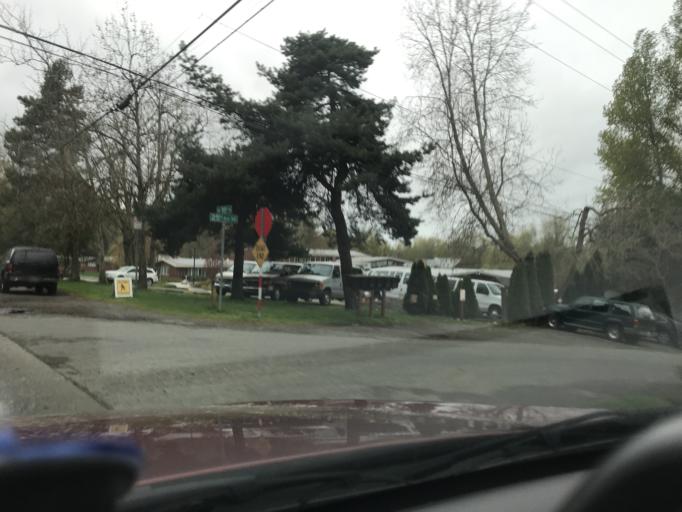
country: US
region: Washington
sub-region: King County
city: Lake Forest Park
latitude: 47.6976
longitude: -122.3012
